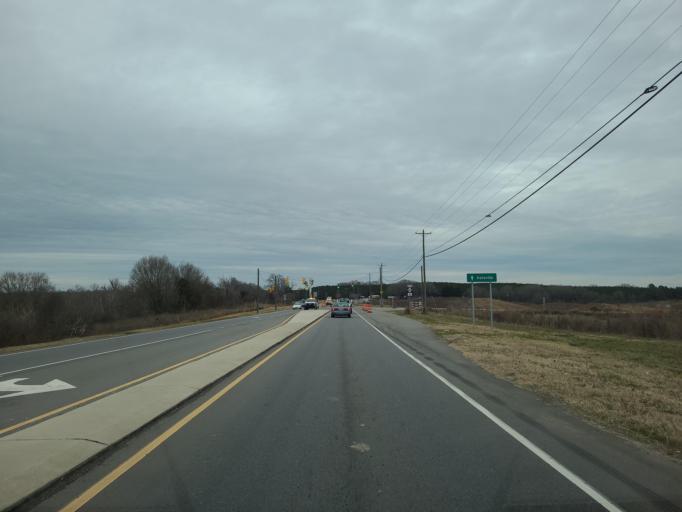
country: US
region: North Carolina
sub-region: Cleveland County
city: Shelby
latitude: 35.3153
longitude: -81.5703
